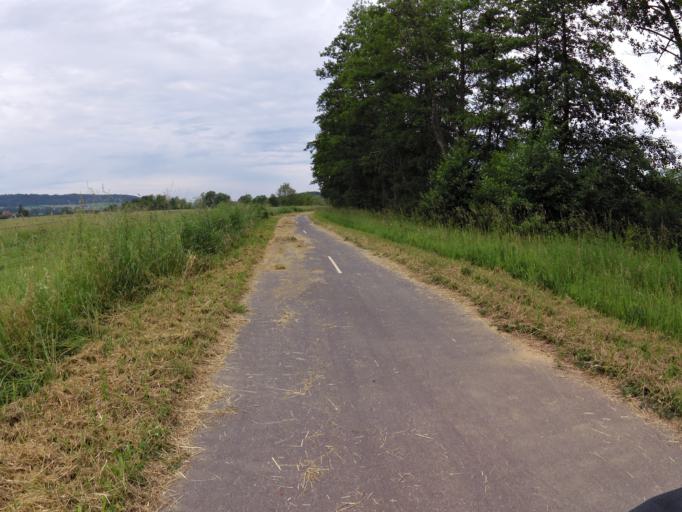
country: FR
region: Champagne-Ardenne
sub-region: Departement des Ardennes
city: Donchery
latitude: 49.6971
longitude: 4.8403
